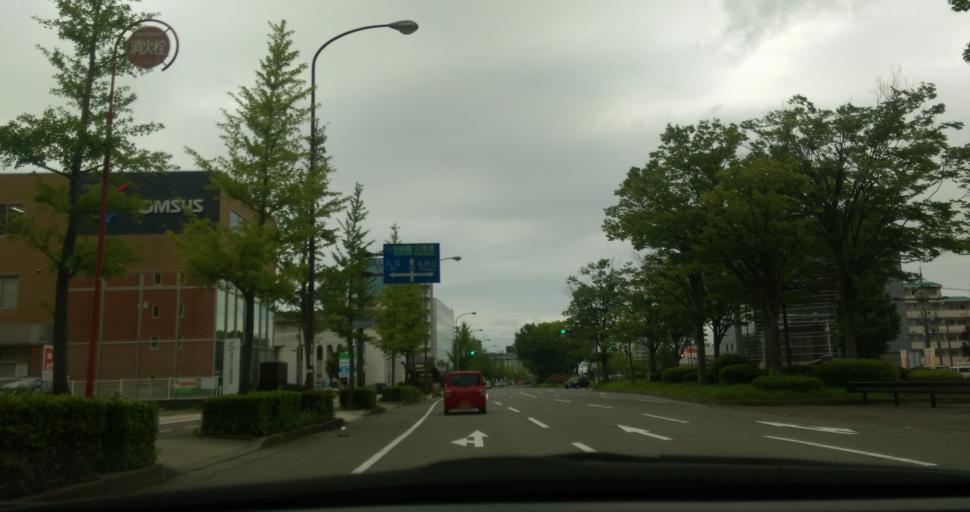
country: JP
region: Ishikawa
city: Kanazawa-shi
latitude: 36.5820
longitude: 136.6413
